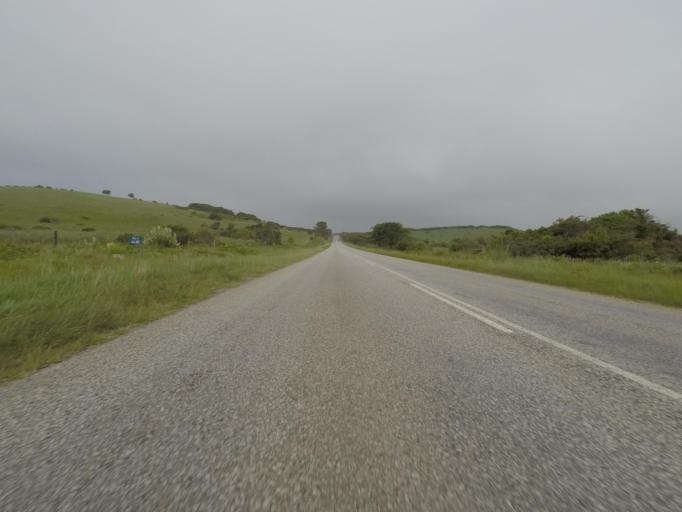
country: ZA
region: Eastern Cape
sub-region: Cacadu District Municipality
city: Port Alfred
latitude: -33.6059
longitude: 26.8340
